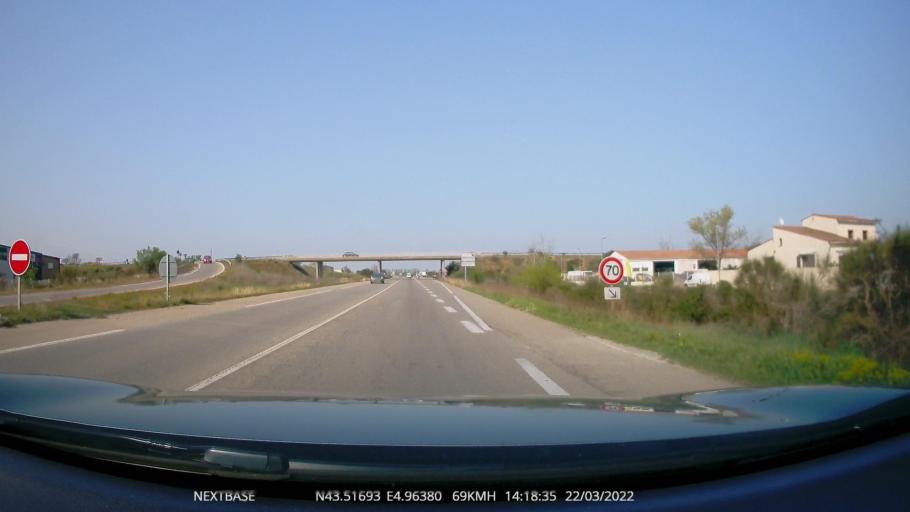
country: FR
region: Provence-Alpes-Cote d'Azur
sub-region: Departement des Bouches-du-Rhone
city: Istres
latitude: 43.5171
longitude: 4.9638
